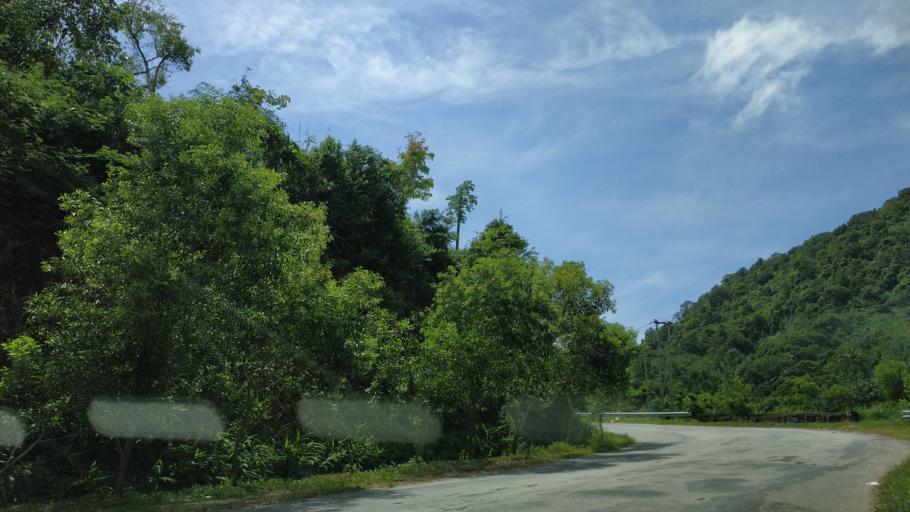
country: MM
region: Tanintharyi
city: Dawei
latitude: 14.1430
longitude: 98.1131
